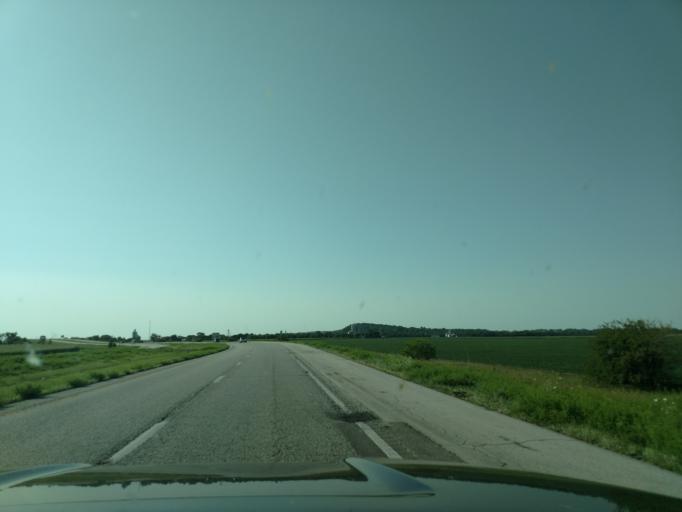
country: US
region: Iowa
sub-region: Fremont County
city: Hamburg
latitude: 40.5818
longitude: -95.6498
